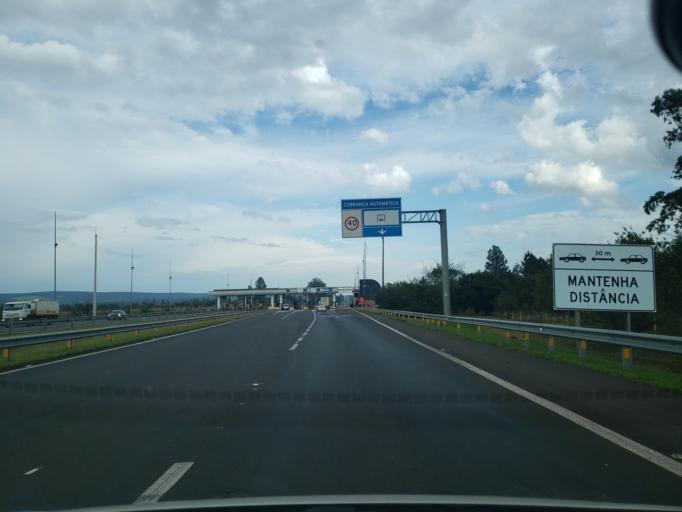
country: BR
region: Sao Paulo
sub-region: Itirapina
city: Itirapina
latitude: -22.2633
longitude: -47.9004
